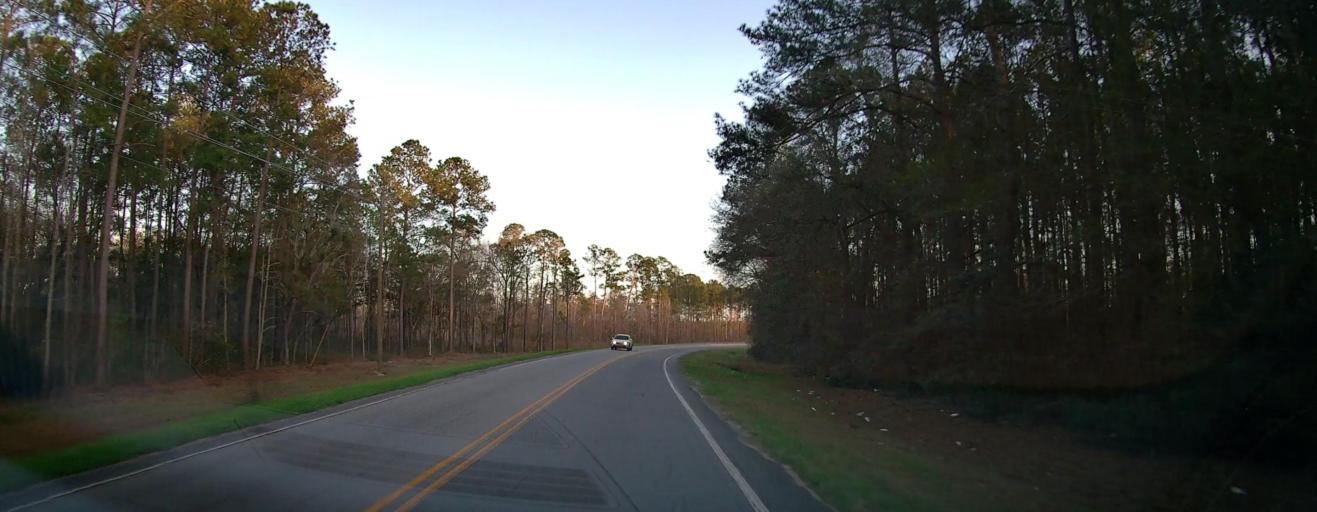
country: US
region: Georgia
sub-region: Chatham County
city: Bloomingdale
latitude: 32.1317
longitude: -81.3870
